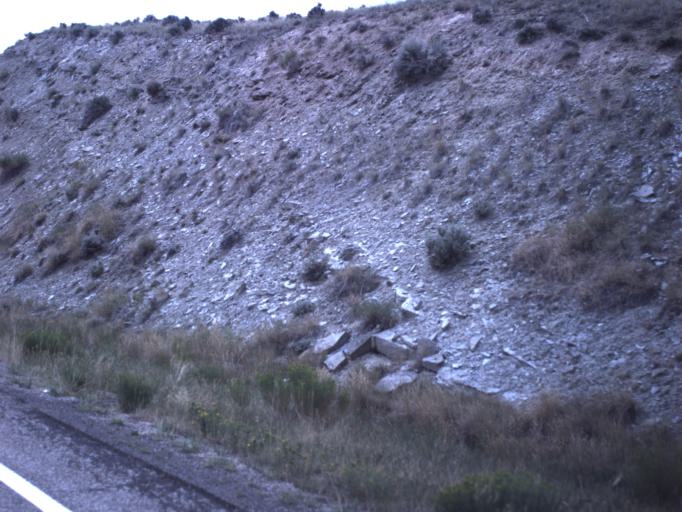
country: US
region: Utah
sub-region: Daggett County
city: Manila
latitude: 40.9175
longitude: -109.6919
